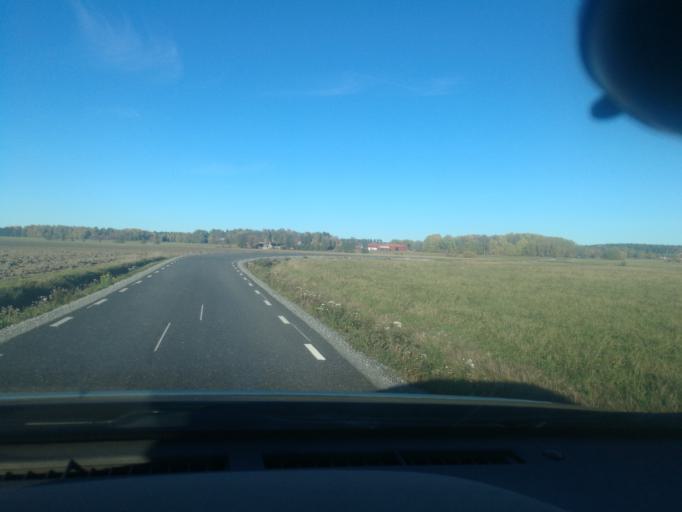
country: SE
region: Vaestmanland
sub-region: Kopings Kommun
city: Koping
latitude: 59.5710
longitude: 16.0766
